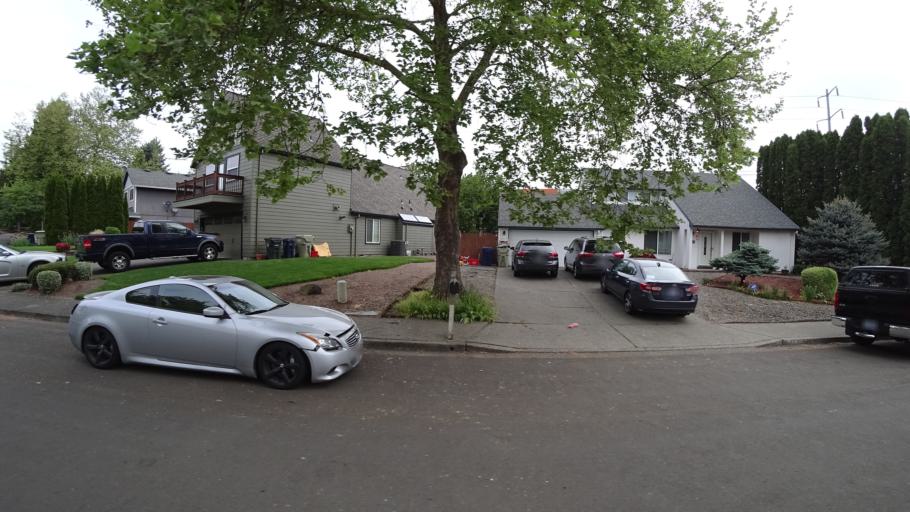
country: US
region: Oregon
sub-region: Washington County
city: Aloha
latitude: 45.5168
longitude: -122.8706
